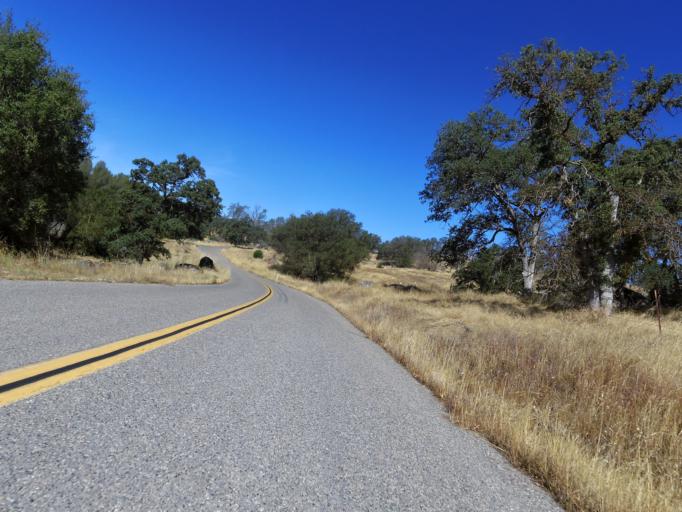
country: US
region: California
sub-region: Madera County
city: Yosemite Lakes
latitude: 37.2581
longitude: -119.9539
